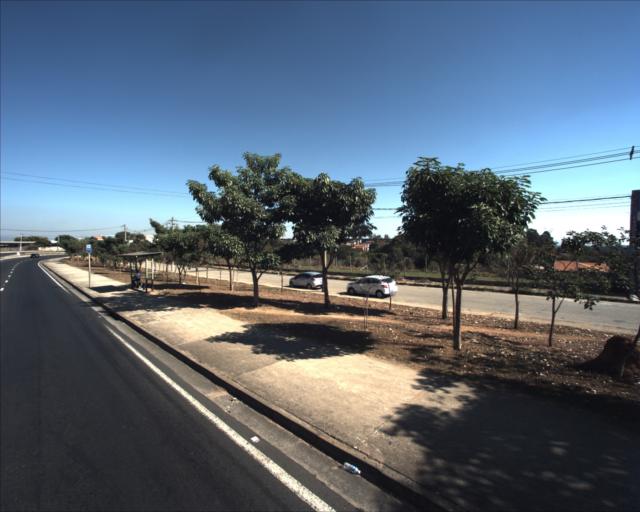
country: BR
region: Sao Paulo
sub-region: Sorocaba
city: Sorocaba
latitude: -23.4033
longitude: -47.3804
